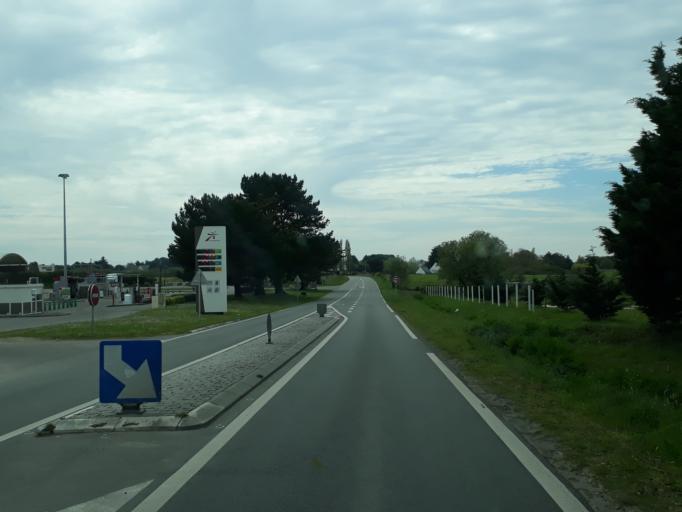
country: FR
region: Pays de la Loire
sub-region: Departement de la Loire-Atlantique
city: Guerande
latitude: 47.3053
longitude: -2.4086
